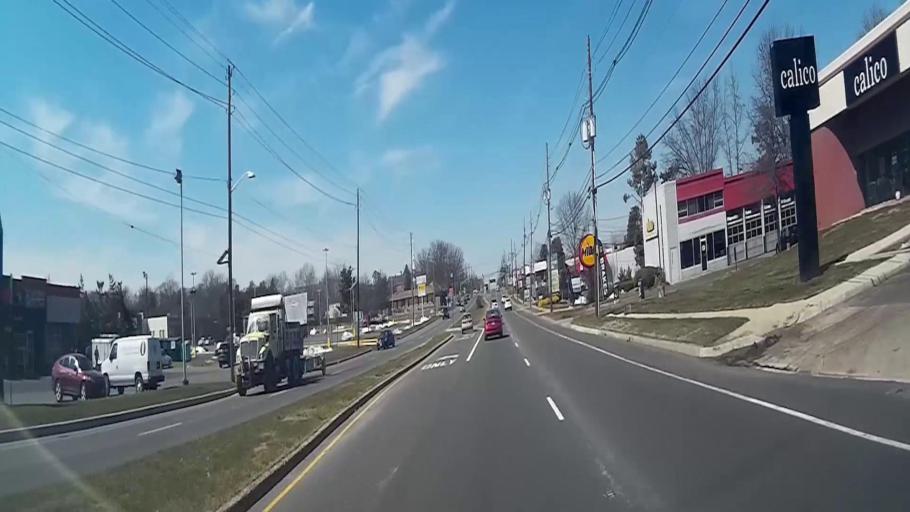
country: US
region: New Jersey
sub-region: Camden County
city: Greentree
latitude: 39.8967
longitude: -74.9491
